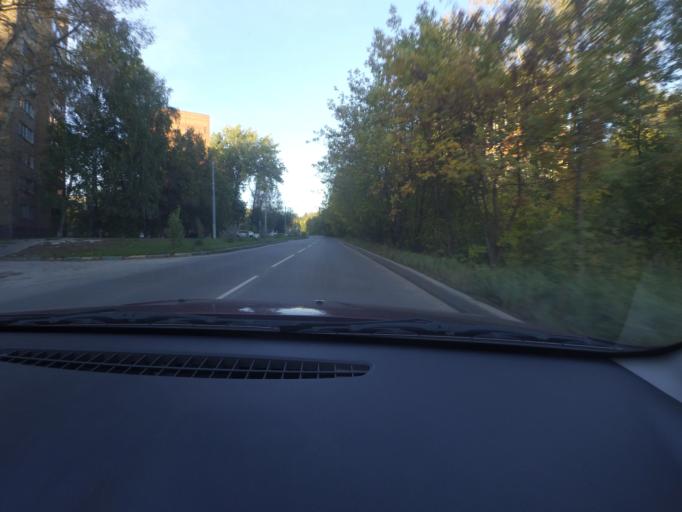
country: RU
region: Nizjnij Novgorod
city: Nizhniy Novgorod
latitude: 56.2796
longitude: 43.9913
